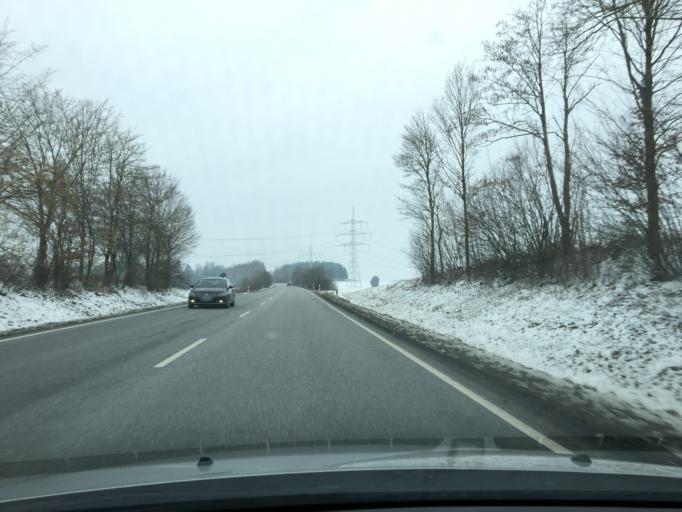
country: DE
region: Bavaria
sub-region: Lower Bavaria
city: Geisenhausen
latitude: 48.4889
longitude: 12.2356
